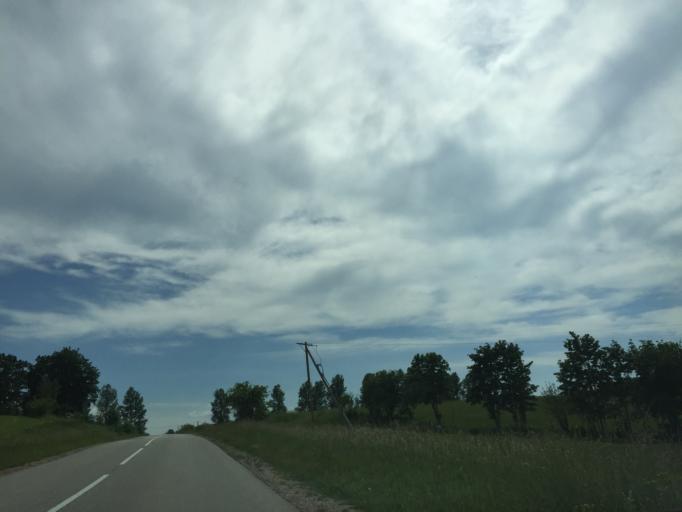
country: LV
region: Engure
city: Smarde
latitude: 57.0336
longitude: 23.2514
